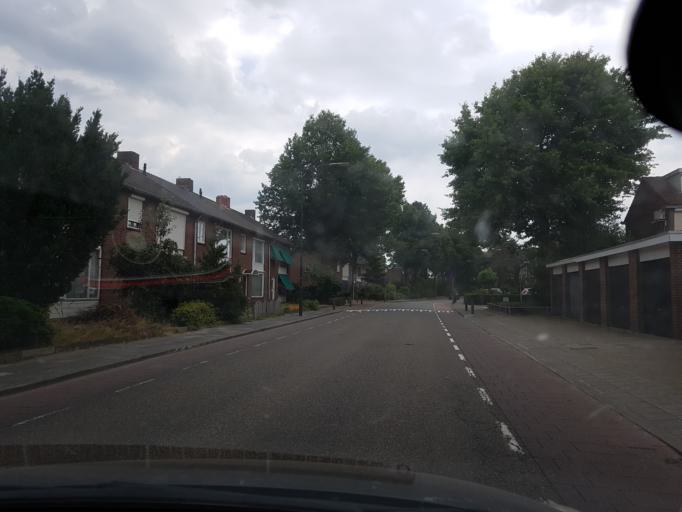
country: NL
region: North Brabant
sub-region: Gemeente Geldrop-Mierlo
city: Geldrop
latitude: 51.4308
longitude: 5.5653
